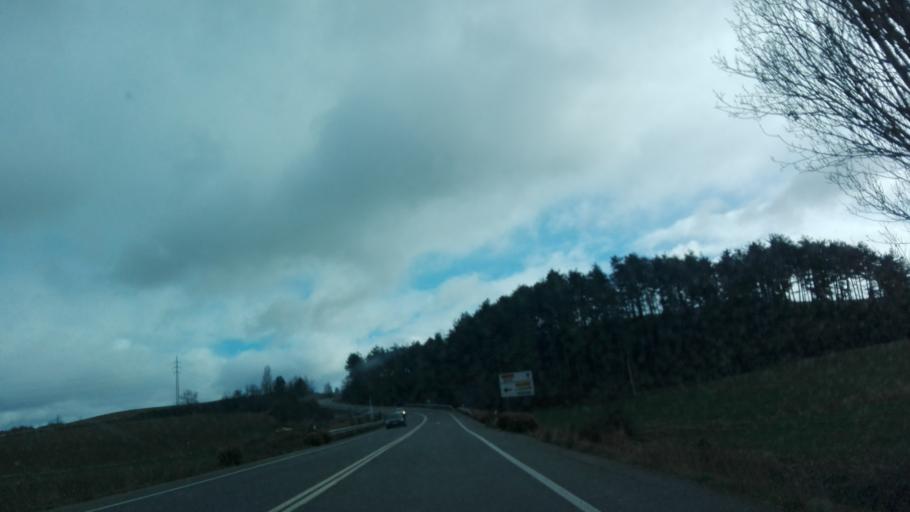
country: ES
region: Navarre
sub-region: Provincia de Navarra
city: Lizoain
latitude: 42.7966
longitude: -1.4836
